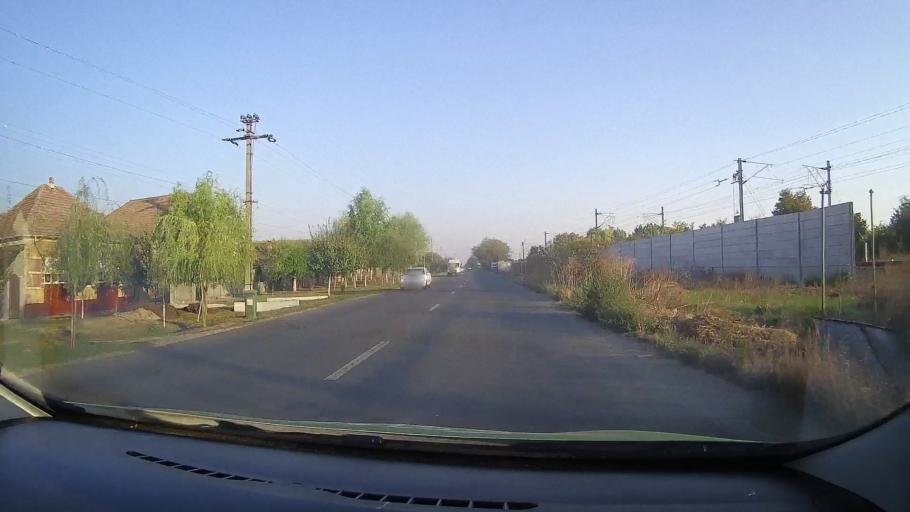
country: RO
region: Arad
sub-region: Comuna Sofronea
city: Sofronea
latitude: 46.2825
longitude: 21.3133
